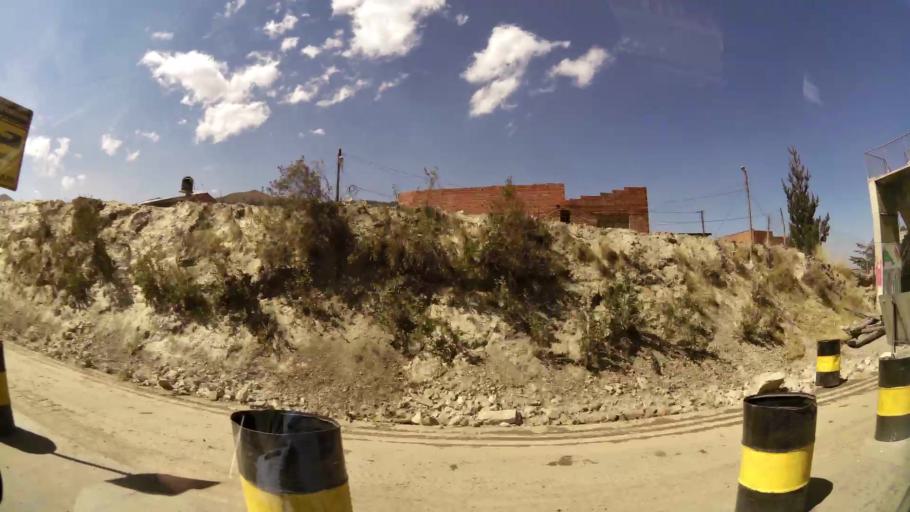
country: BO
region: La Paz
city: La Paz
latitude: -16.4671
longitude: -68.1556
